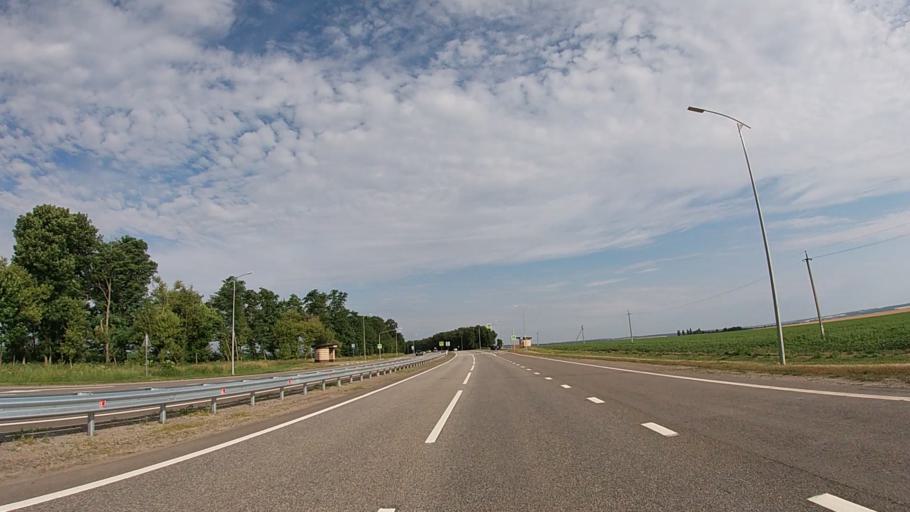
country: RU
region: Belgorod
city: Tomarovka
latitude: 50.6807
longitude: 36.2880
